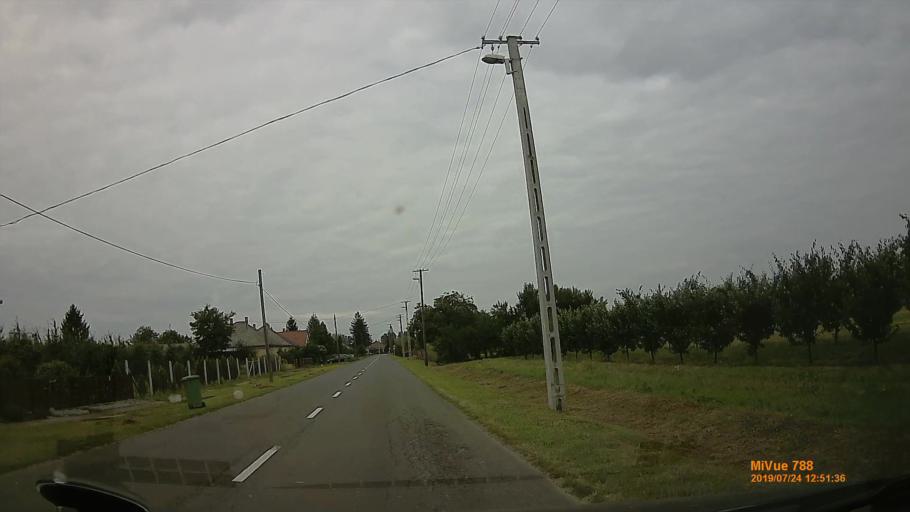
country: HU
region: Szabolcs-Szatmar-Bereg
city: Aranyosapati
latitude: 48.1935
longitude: 22.2987
